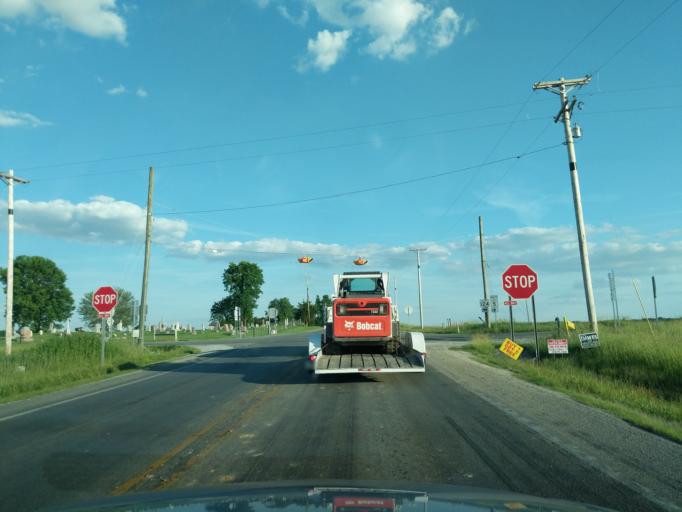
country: US
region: Indiana
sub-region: Huntington County
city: Warren
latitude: 40.7423
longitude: -85.4446
